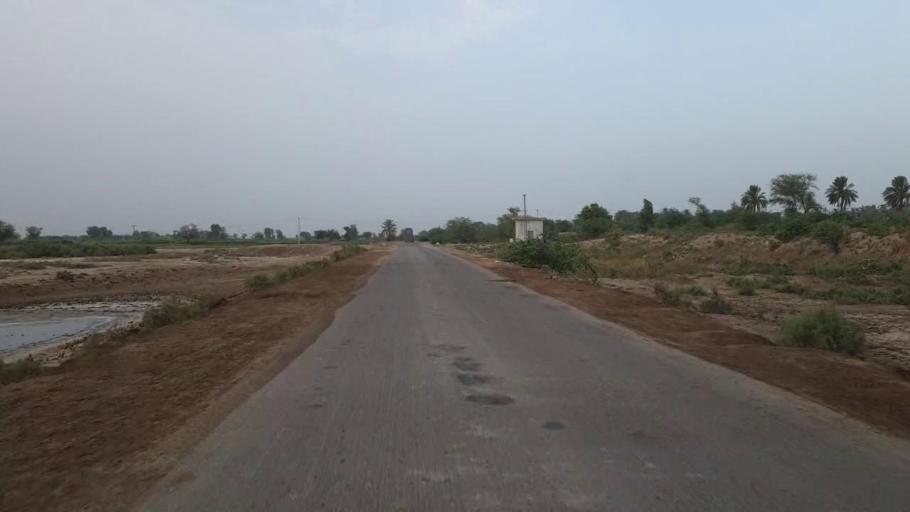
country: PK
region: Sindh
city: Daur
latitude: 26.4331
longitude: 68.2683
